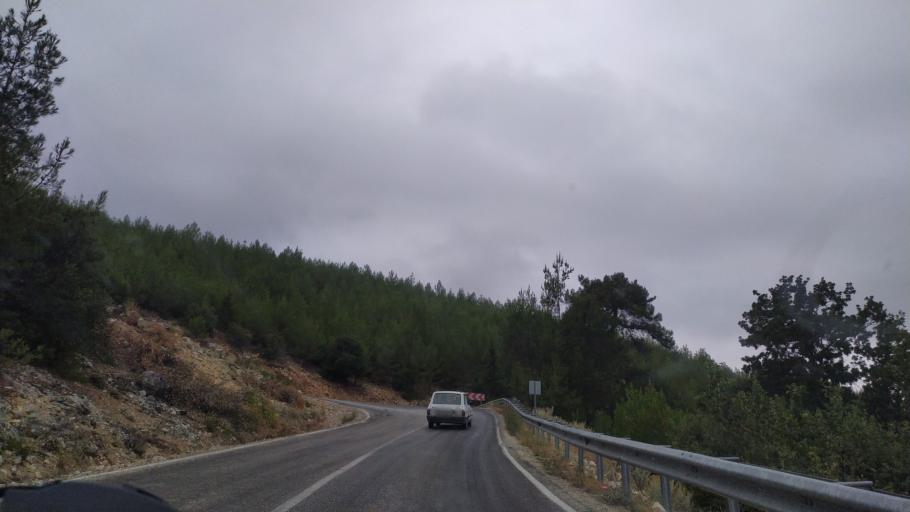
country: TR
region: Mersin
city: Silifke
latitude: 36.5429
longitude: 33.9298
